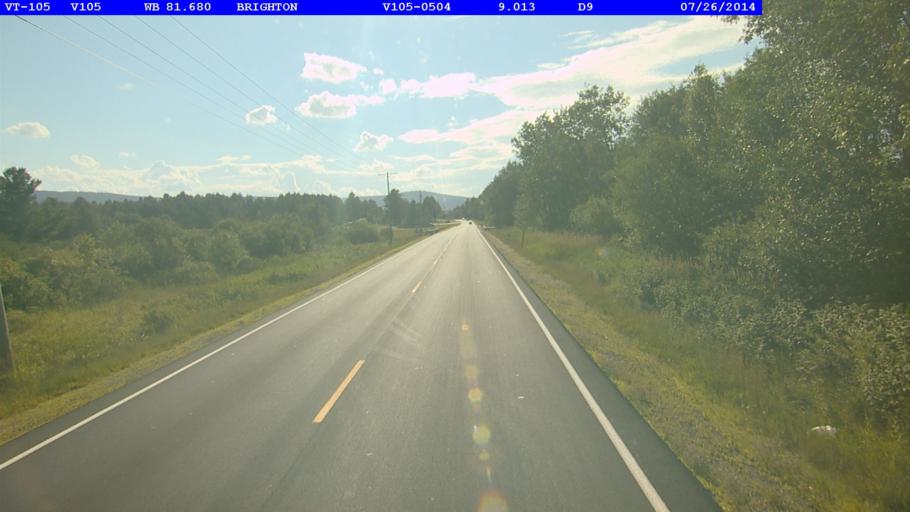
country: US
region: New Hampshire
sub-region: Coos County
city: Stratford
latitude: 44.7860
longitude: -71.8076
